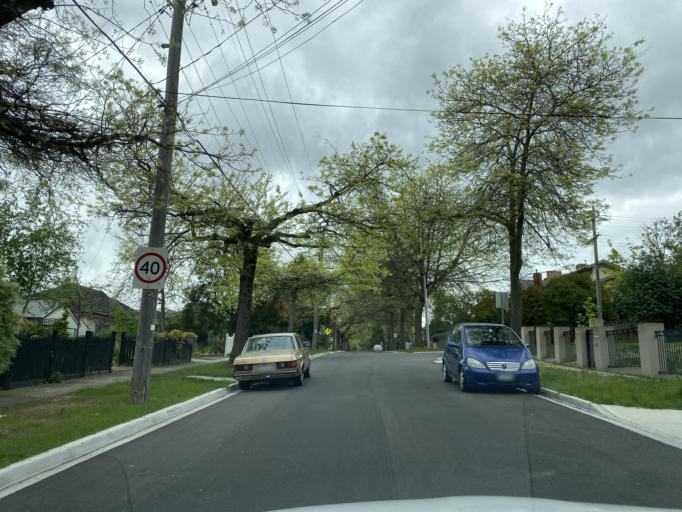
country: AU
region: Victoria
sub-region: Whitehorse
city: Box Hill South
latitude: -37.8332
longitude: 145.1267
